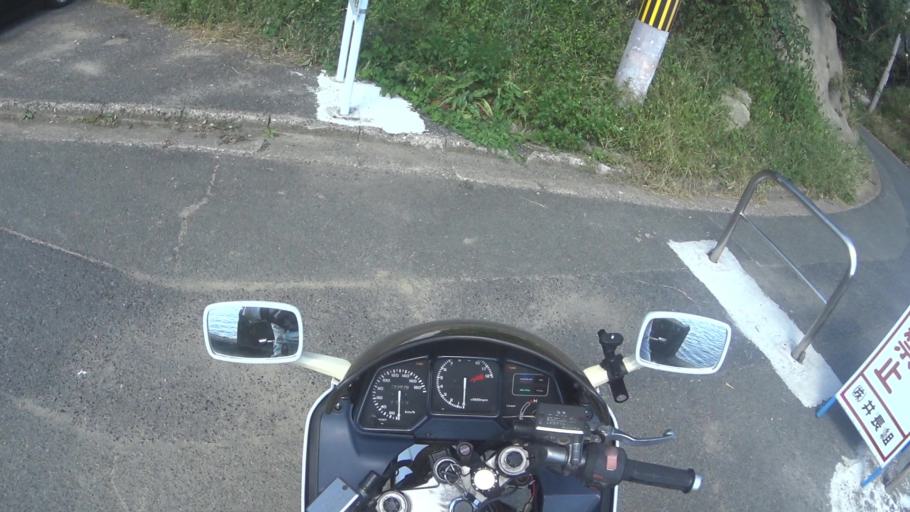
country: JP
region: Kyoto
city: Miyazu
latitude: 35.6643
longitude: 135.2894
